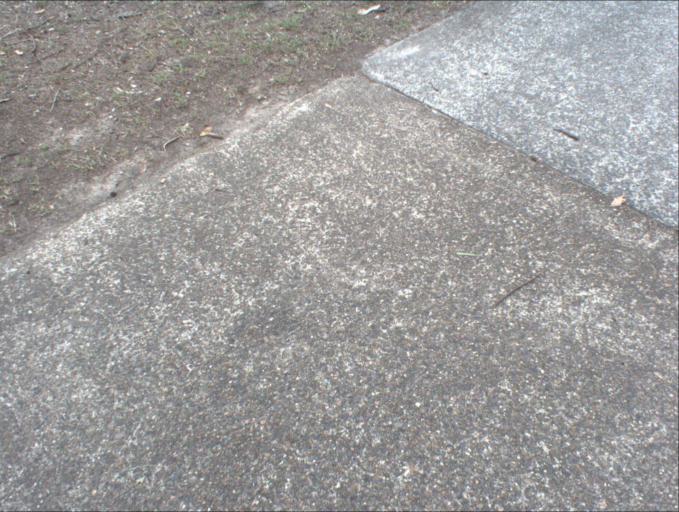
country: AU
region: Queensland
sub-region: Logan
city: Park Ridge South
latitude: -27.6917
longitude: 153.0254
